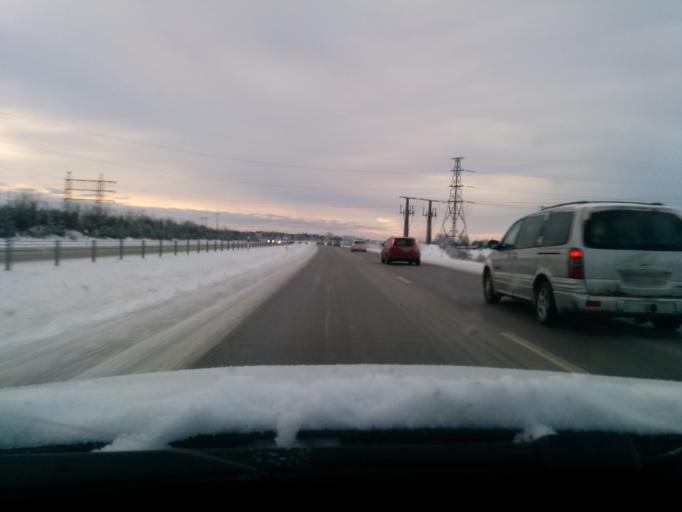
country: SE
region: Uppsala
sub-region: Uppsala Kommun
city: Gamla Uppsala
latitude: 59.9162
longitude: 17.6515
